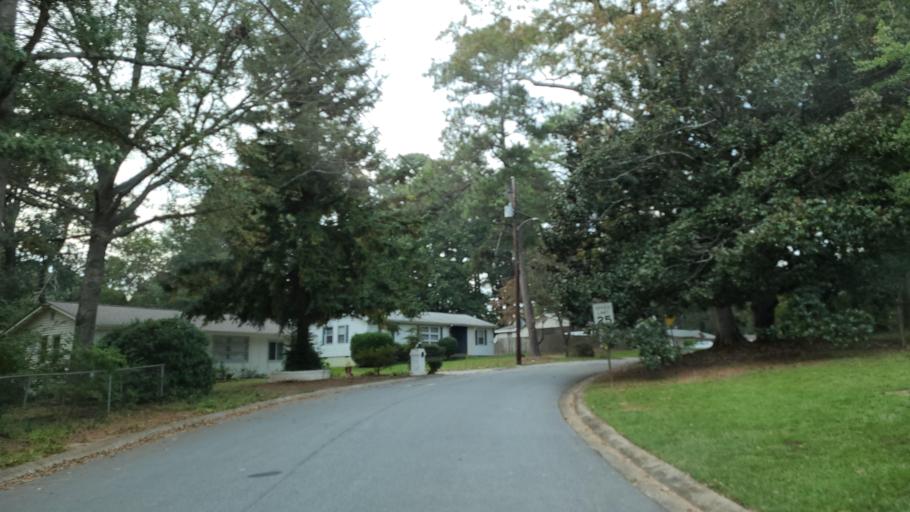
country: US
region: Georgia
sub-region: Cobb County
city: Smyrna
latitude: 33.8852
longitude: -84.5388
